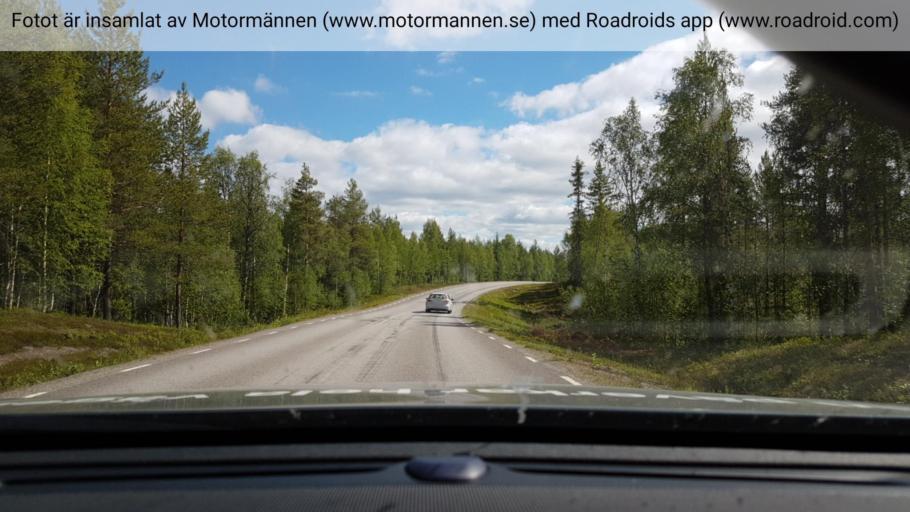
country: SE
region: Vaesterbotten
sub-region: Sorsele Kommun
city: Sorsele
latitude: 65.5928
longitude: 17.5061
